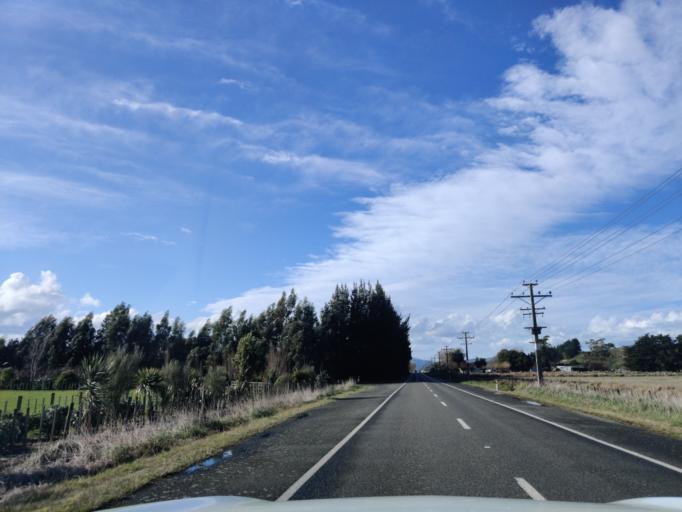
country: NZ
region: Manawatu-Wanganui
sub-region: Palmerston North City
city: Palmerston North
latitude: -40.3609
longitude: 175.6775
